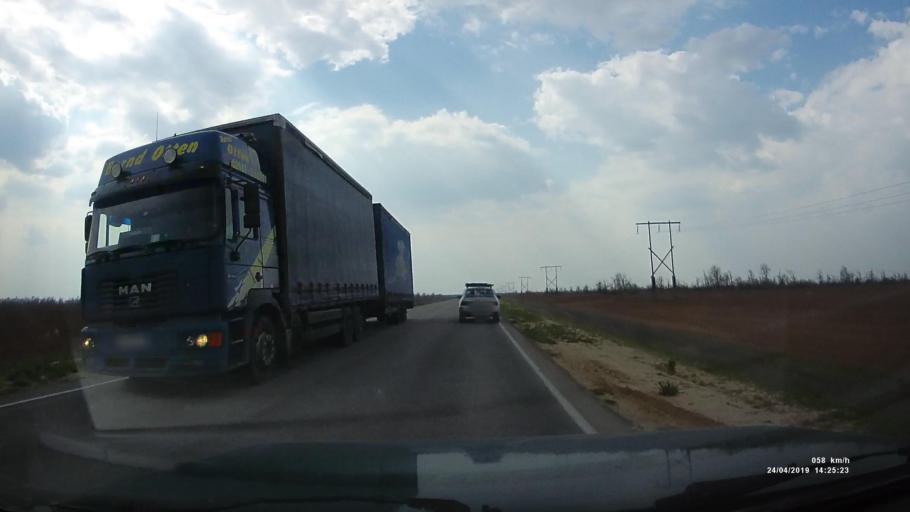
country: RU
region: Kalmykiya
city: Arshan'
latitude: 46.3305
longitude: 44.0820
